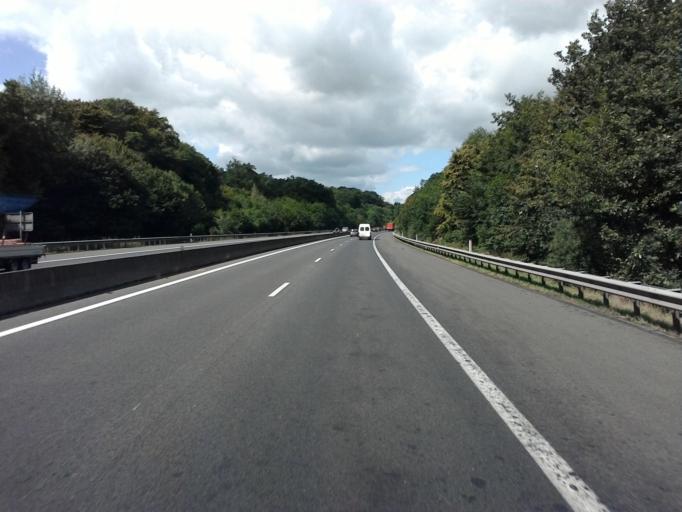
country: LU
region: Luxembourg
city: Capellen
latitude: 49.6350
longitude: 5.9907
